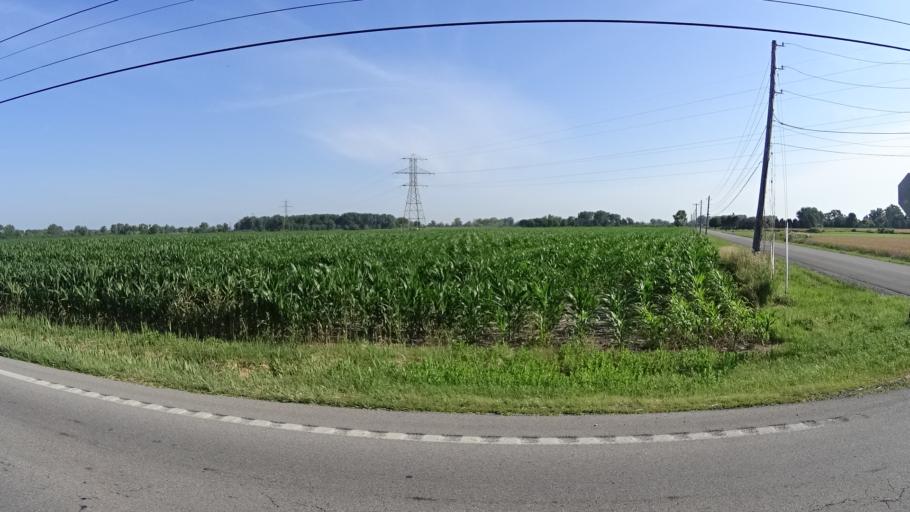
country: US
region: Ohio
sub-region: Erie County
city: Sandusky
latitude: 41.4421
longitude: -82.8029
